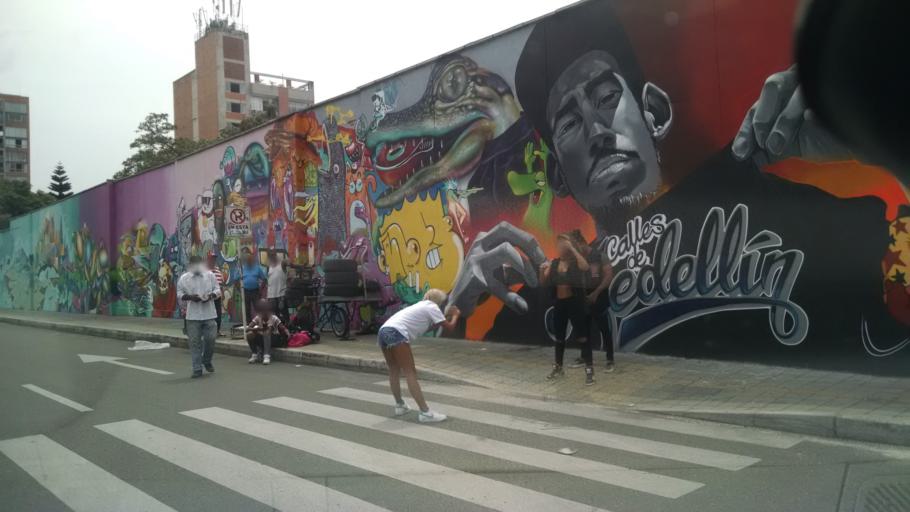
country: CO
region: Antioquia
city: Itagui
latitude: 6.2104
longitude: -75.5722
